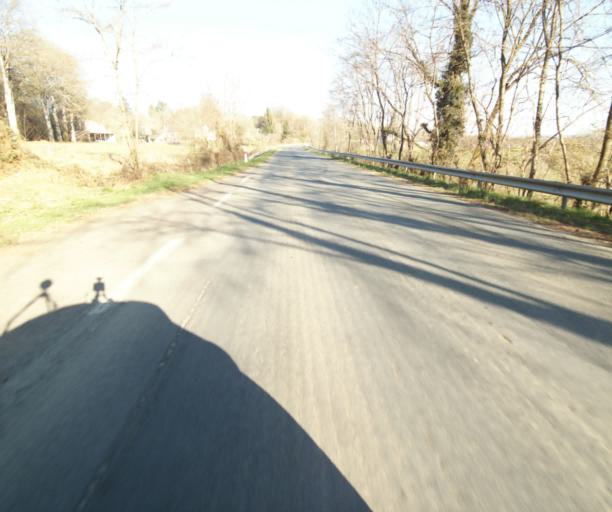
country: FR
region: Limousin
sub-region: Departement de la Correze
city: Uzerche
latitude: 45.3907
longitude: 1.5964
